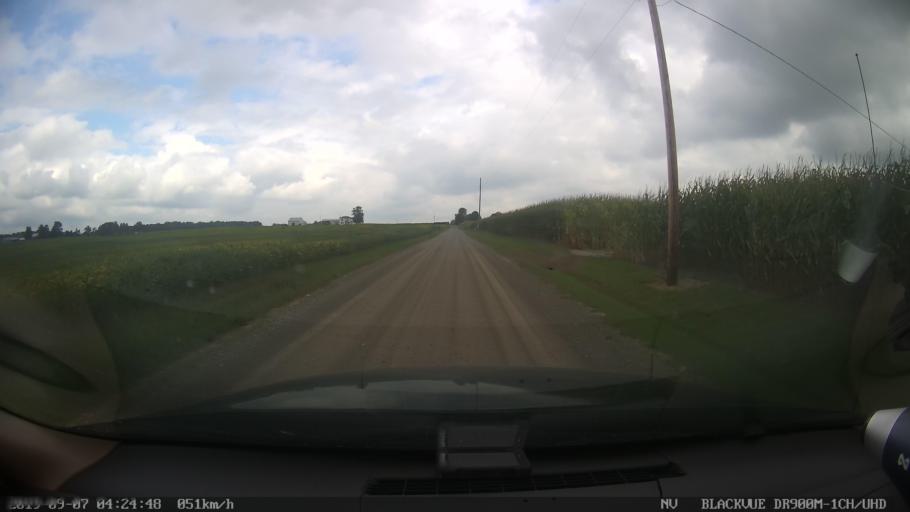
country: US
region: Ohio
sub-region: Knox County
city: Centerburg
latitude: 40.2902
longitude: -82.6690
